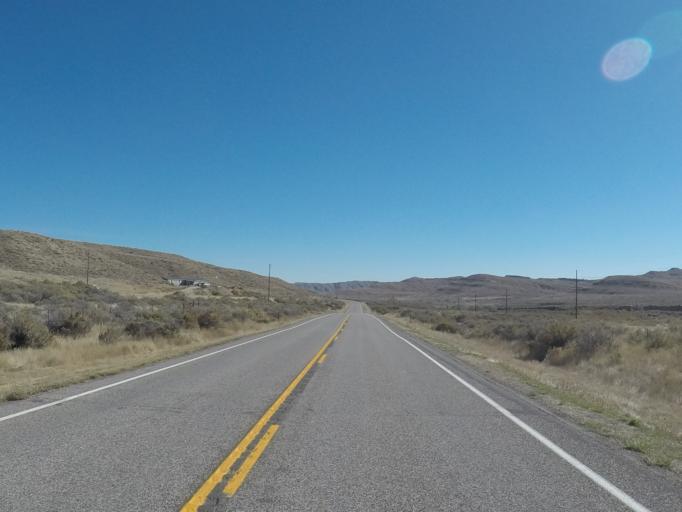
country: US
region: Montana
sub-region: Carbon County
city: Red Lodge
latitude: 45.1476
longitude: -109.0509
